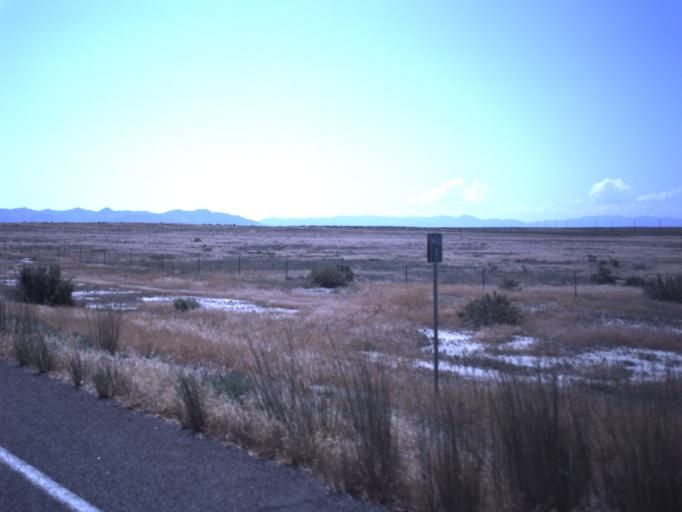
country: US
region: Utah
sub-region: Millard County
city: Delta
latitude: 39.4910
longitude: -112.5605
